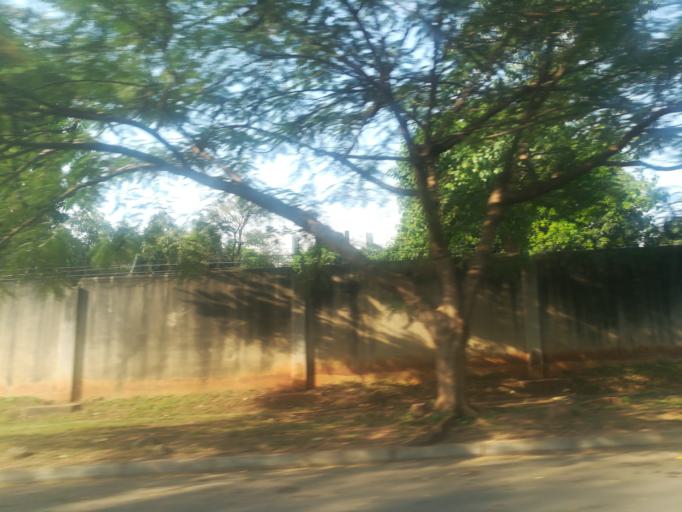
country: NG
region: Abuja Federal Capital Territory
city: Abuja
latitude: 9.0609
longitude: 7.4508
